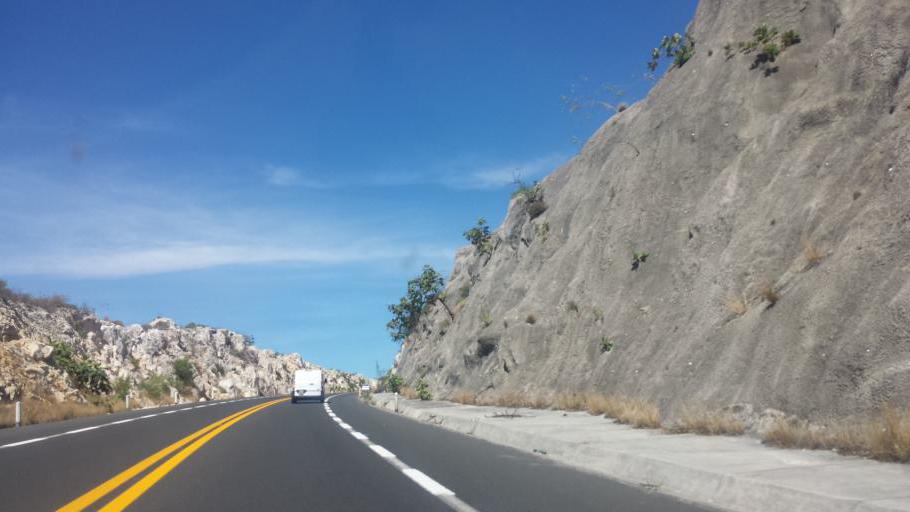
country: MX
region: Oaxaca
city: San Gabriel Casa Blanca
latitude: 17.9895
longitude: -97.3547
